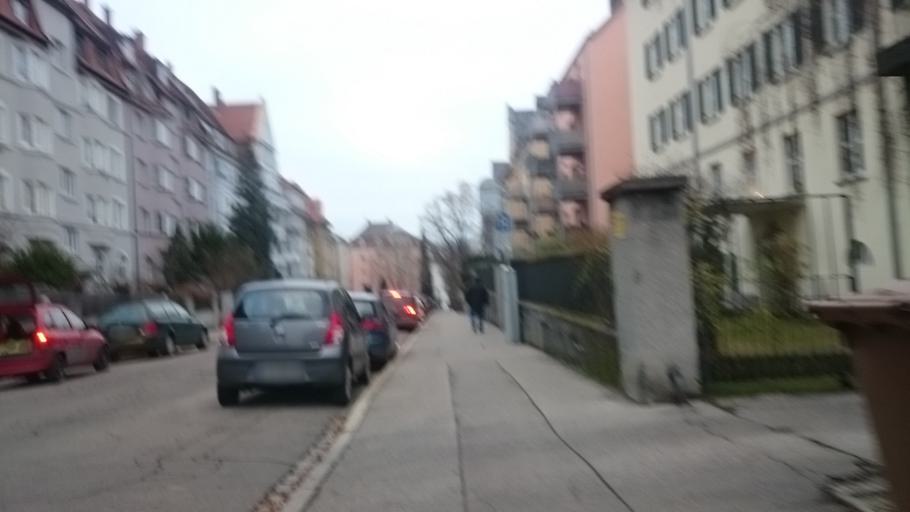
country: DE
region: Bavaria
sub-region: Swabia
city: Augsburg
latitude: 48.3779
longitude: 10.8931
